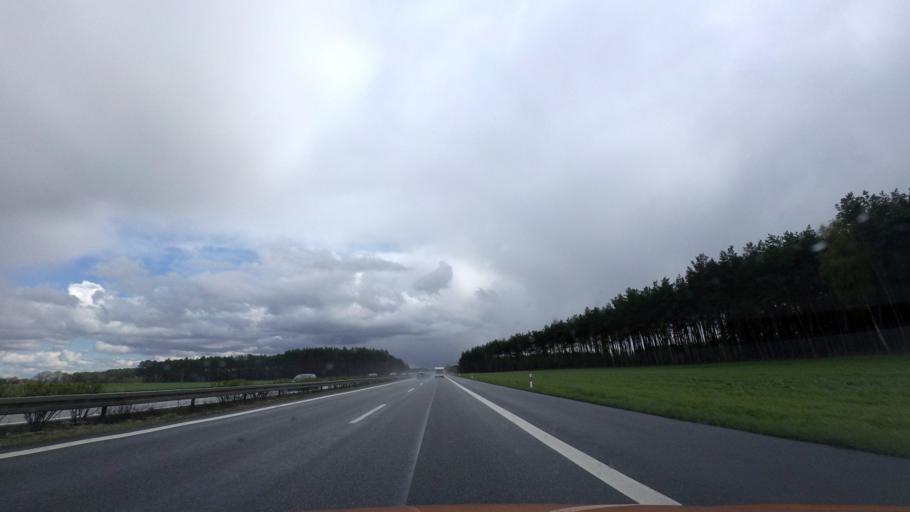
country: DE
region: Mecklenburg-Vorpommern
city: Sulstorf
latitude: 53.4560
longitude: 11.3545
